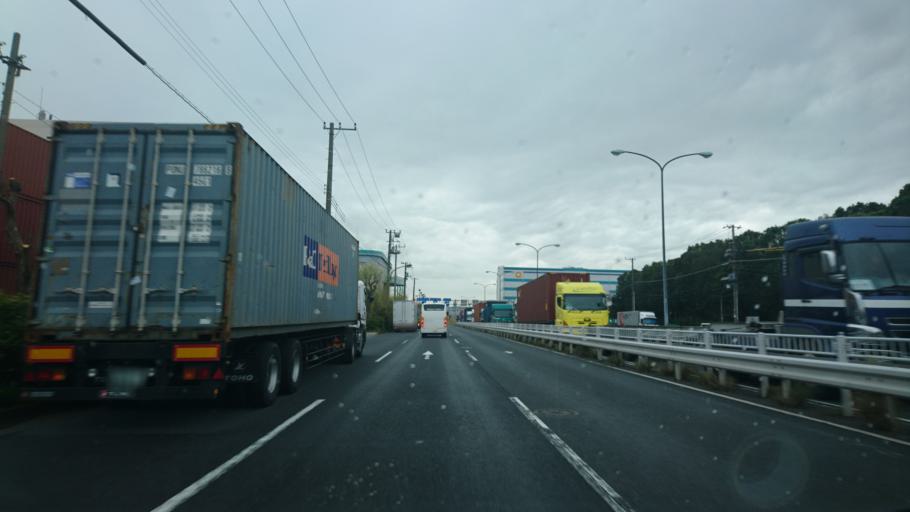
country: JP
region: Kanagawa
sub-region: Kawasaki-shi
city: Kawasaki
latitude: 35.5966
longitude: 139.7639
